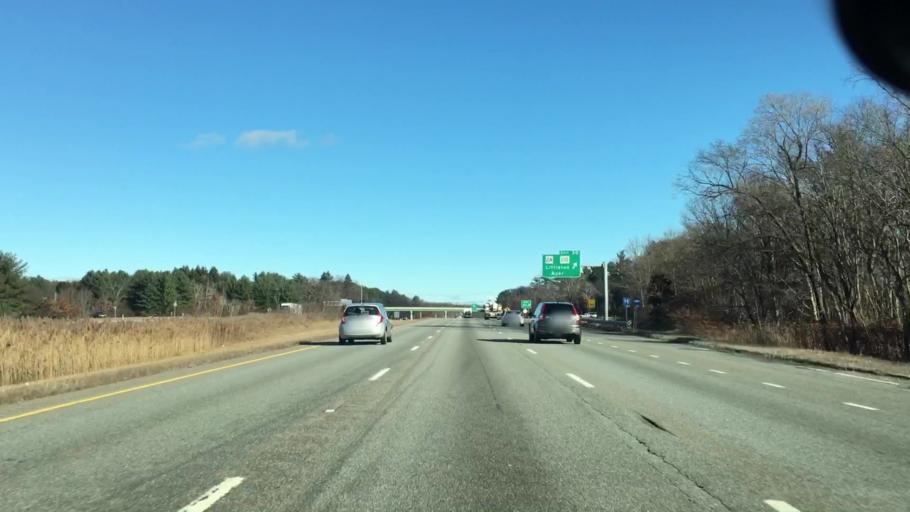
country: US
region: Massachusetts
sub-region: Middlesex County
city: Littleton Common
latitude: 42.5358
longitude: -71.4958
